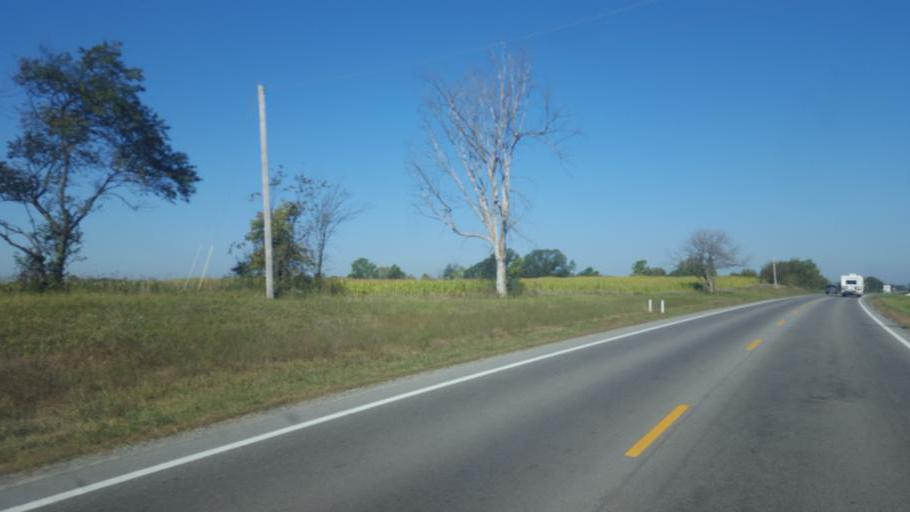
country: US
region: Ohio
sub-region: Hardin County
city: Kenton
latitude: 40.5522
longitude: -83.5357
